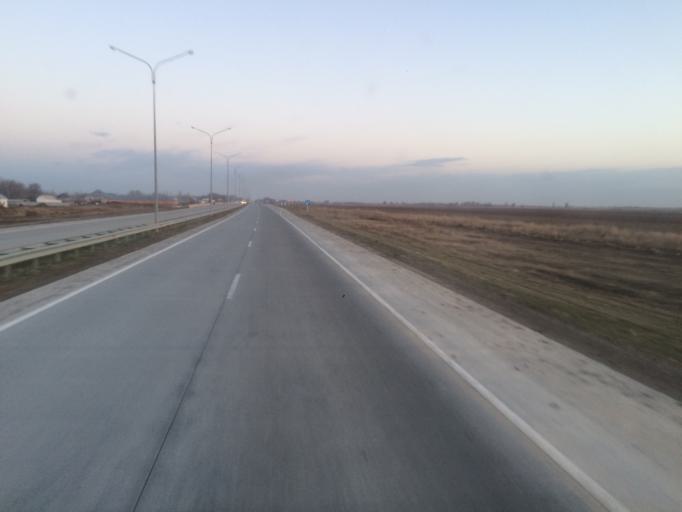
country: KZ
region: Ongtustik Qazaqstan
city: Shayan
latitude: 42.9652
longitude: 68.8813
